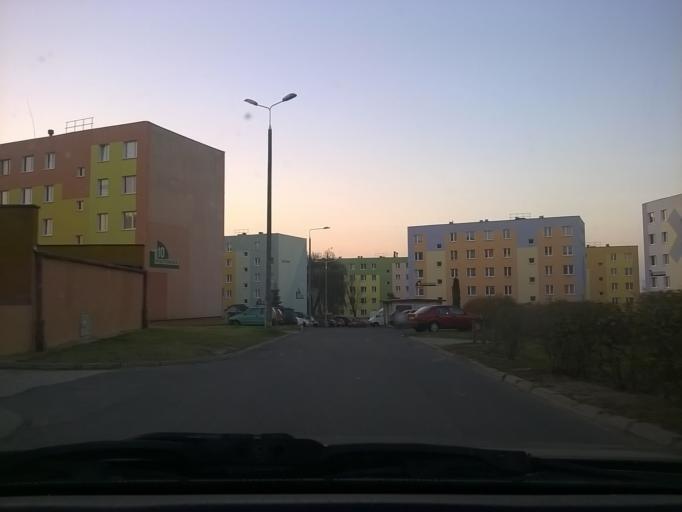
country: PL
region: Warmian-Masurian Voivodeship
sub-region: Powiat ketrzynski
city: Ketrzyn
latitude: 54.0914
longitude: 21.3752
